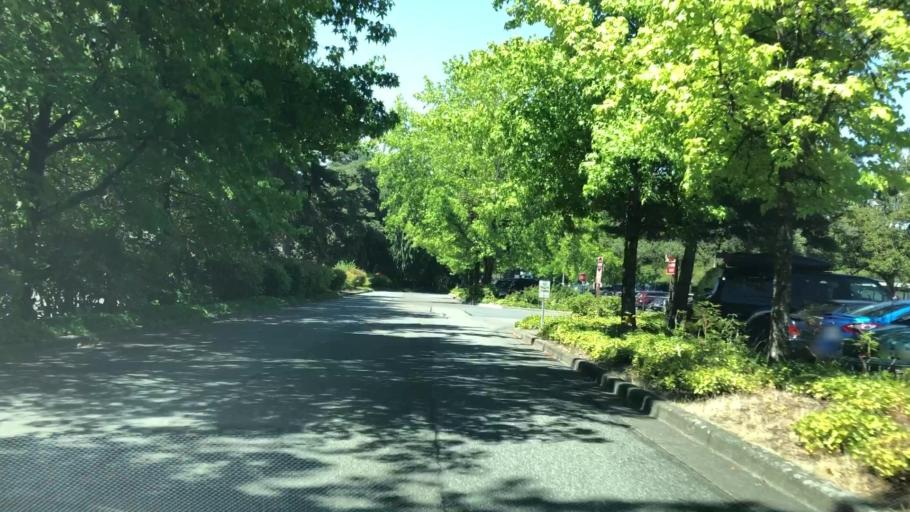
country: US
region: Washington
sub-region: King County
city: Woodinville
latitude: 47.7564
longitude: -122.1509
